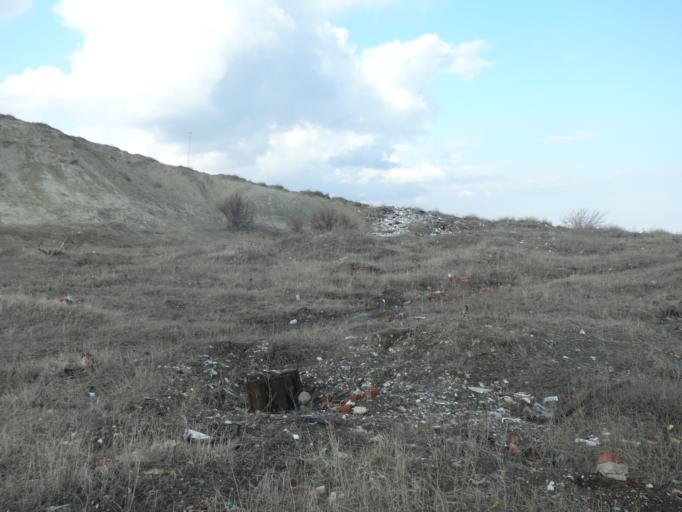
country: RU
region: Saratov
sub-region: Saratovskiy Rayon
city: Saratov
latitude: 51.5496
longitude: 45.9905
